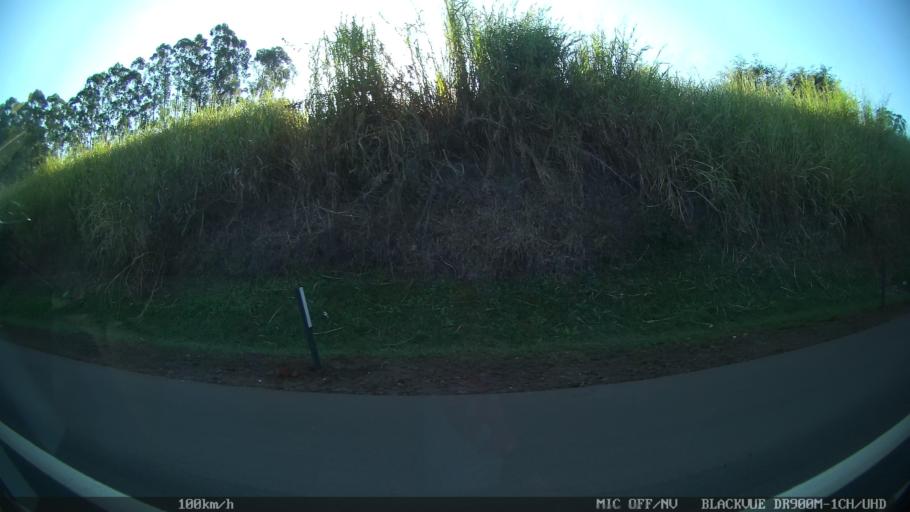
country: BR
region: Sao Paulo
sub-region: Piracicaba
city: Piracicaba
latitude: -22.6990
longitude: -47.6399
